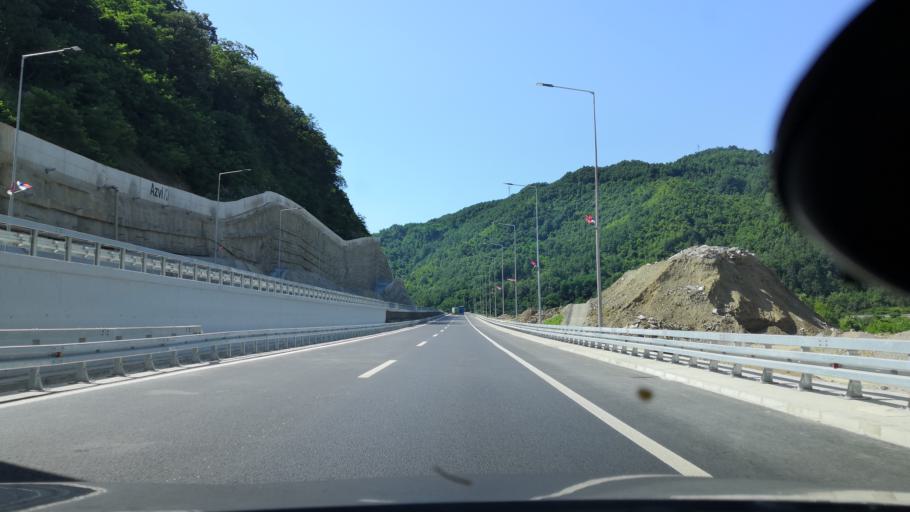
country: RS
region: Central Serbia
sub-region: Jablanicki Okrug
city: Vlasotince
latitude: 42.8686
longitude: 22.1048
